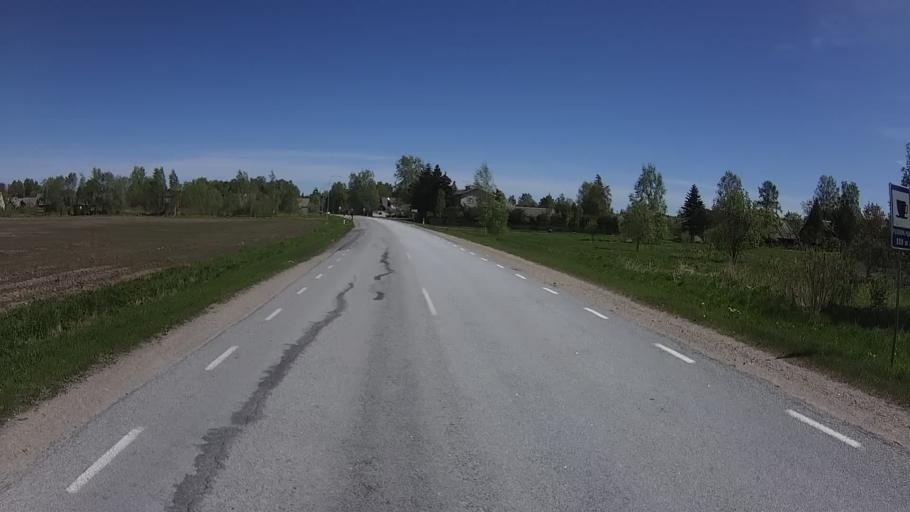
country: EE
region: Polvamaa
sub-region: Raepina vald
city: Rapina
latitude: 58.0897
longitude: 27.4542
